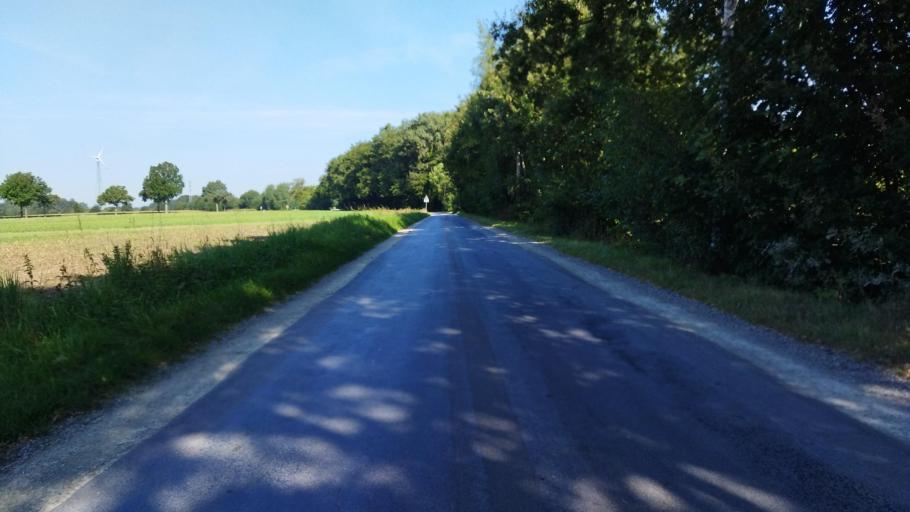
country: DE
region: Lower Saxony
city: Bad Iburg
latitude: 52.1209
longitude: 8.0285
